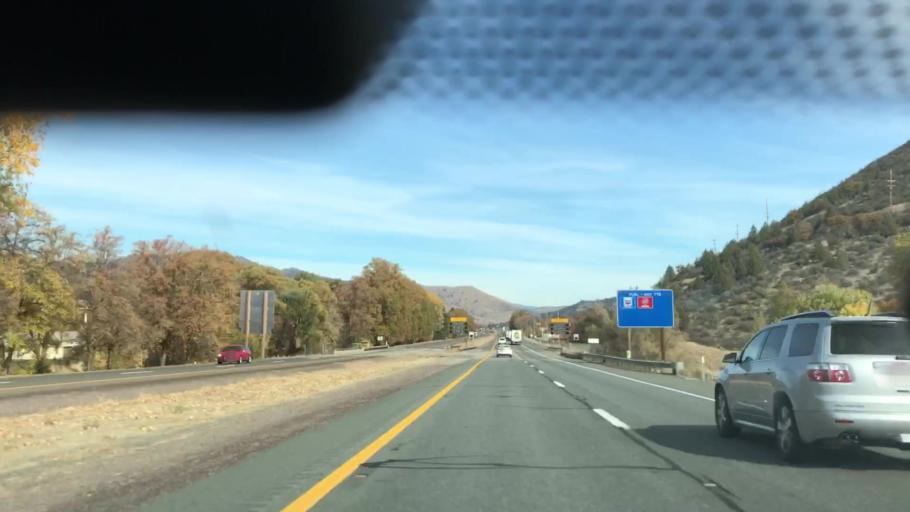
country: US
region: California
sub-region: Siskiyou County
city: Yreka
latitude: 41.7193
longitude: -122.6381
